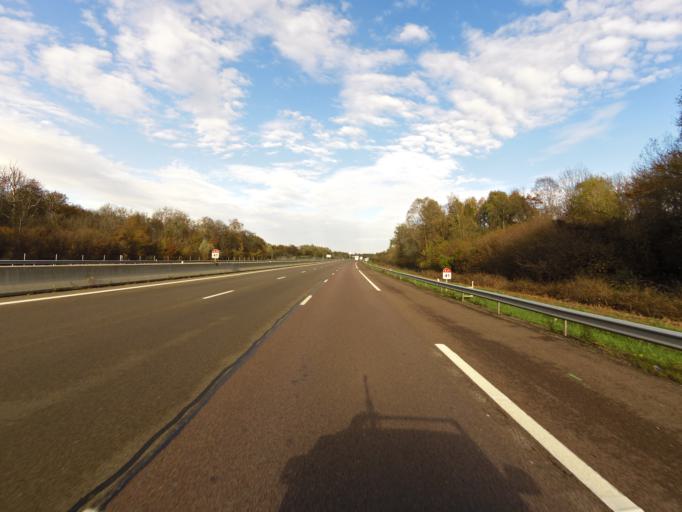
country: FR
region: Bourgogne
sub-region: Departement de la Cote-d'Or
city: Chevigny-Saint-Sauveur
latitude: 47.2904
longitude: 5.1605
